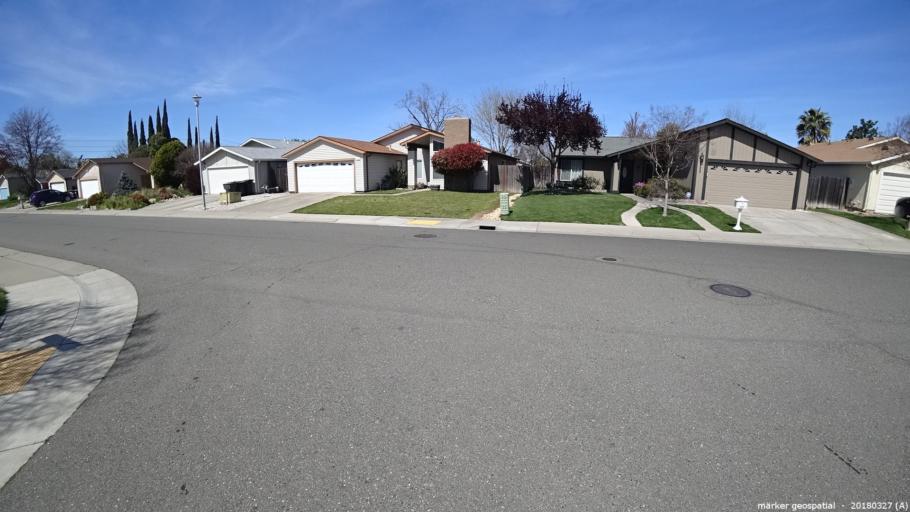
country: US
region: California
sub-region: Sacramento County
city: Rosemont
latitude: 38.5481
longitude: -121.3426
